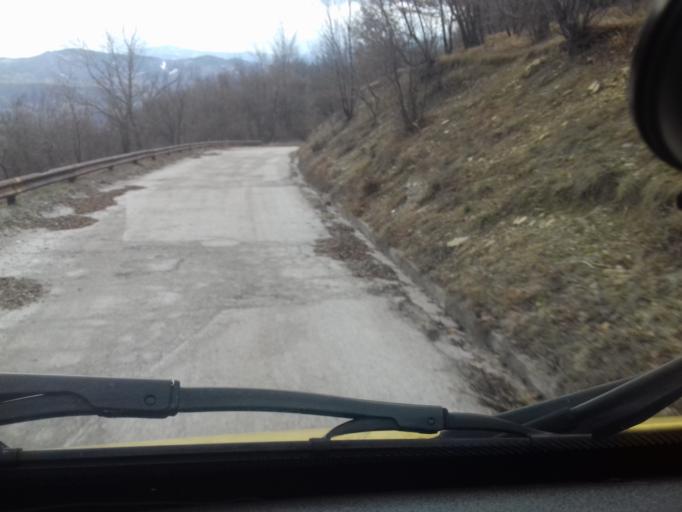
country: BA
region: Federation of Bosnia and Herzegovina
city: Zenica
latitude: 44.2232
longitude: 17.9388
